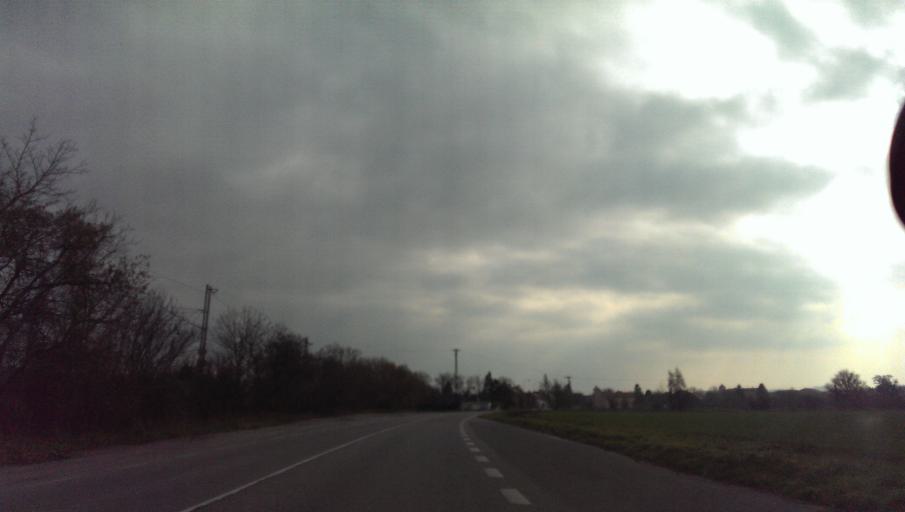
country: CZ
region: Zlin
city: Tlumacov
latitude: 49.2613
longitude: 17.4960
